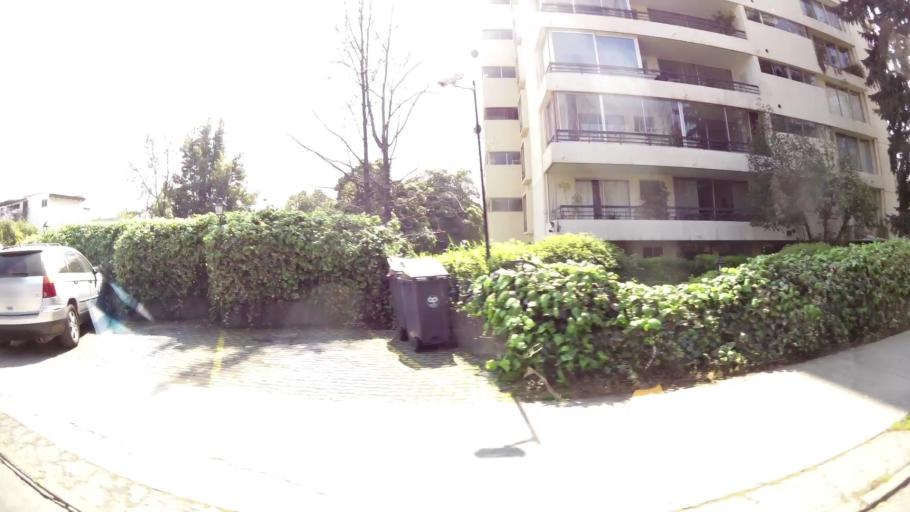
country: CL
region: Santiago Metropolitan
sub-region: Provincia de Santiago
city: Villa Presidente Frei, Nunoa, Santiago, Chile
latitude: -33.3850
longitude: -70.5798
